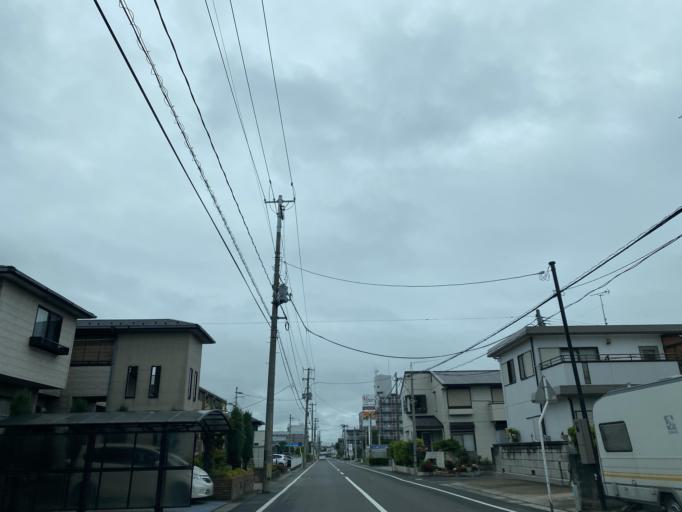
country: JP
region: Fukushima
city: Koriyama
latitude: 37.3932
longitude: 140.3274
